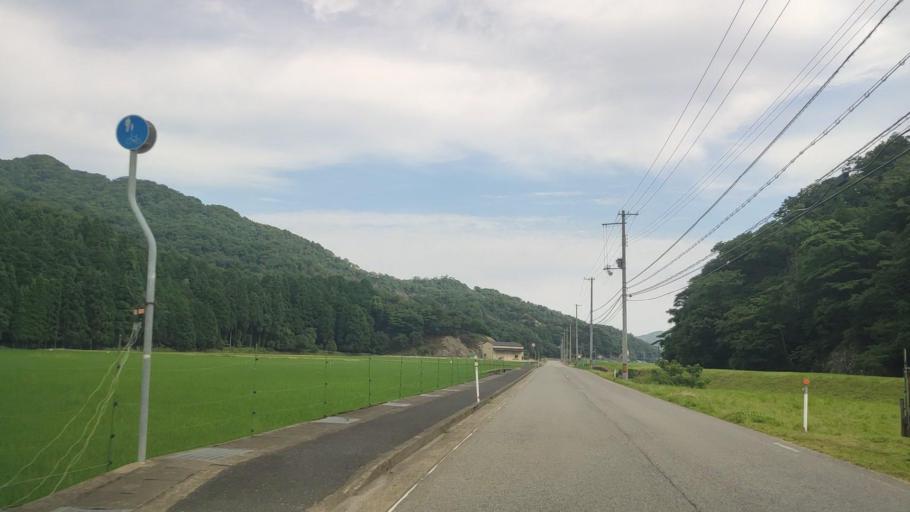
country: JP
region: Hyogo
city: Toyooka
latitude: 35.6178
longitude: 134.8428
